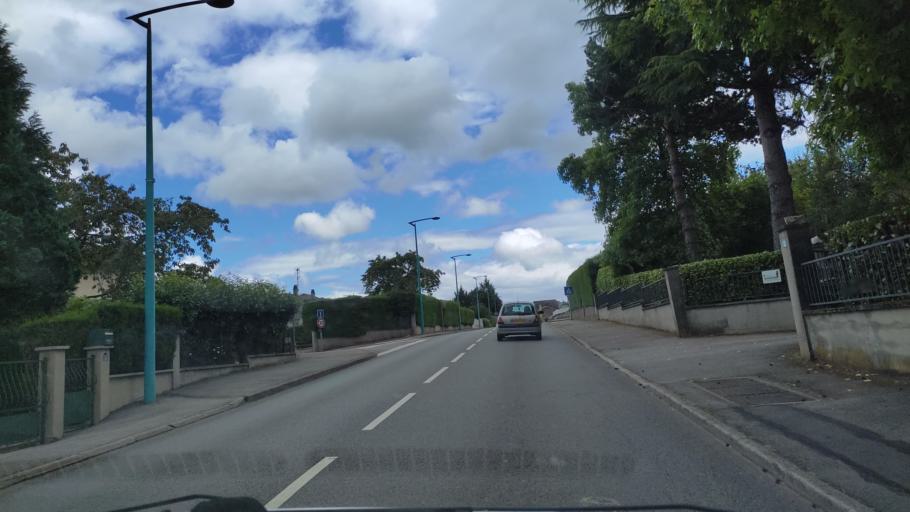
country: FR
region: Limousin
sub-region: Departement de la Haute-Vienne
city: Rilhac-Rancon
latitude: 45.9003
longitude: 1.3132
